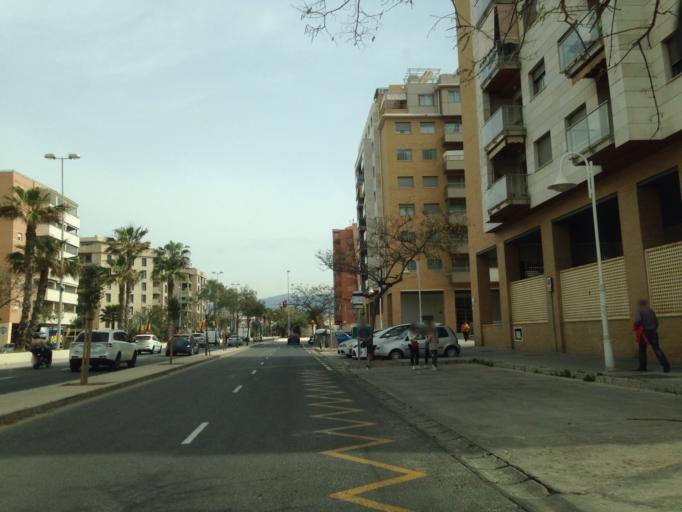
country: ES
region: Andalusia
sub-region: Provincia de Malaga
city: Malaga
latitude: 36.6930
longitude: -4.4409
